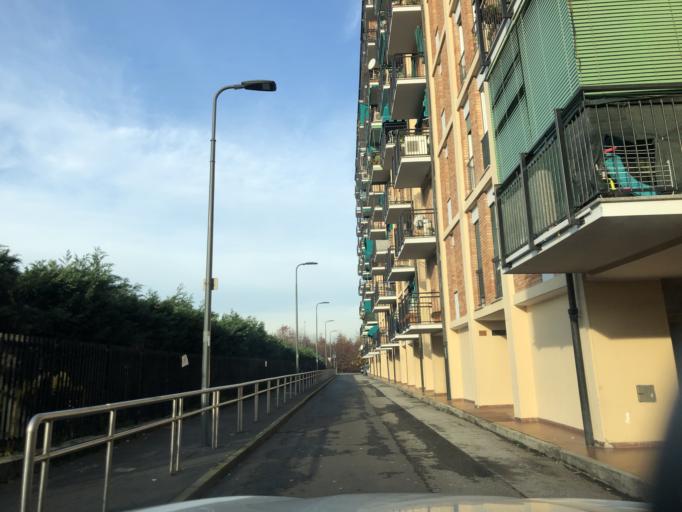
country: IT
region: Lombardy
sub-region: Citta metropolitana di Milano
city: Baranzate
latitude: 45.4928
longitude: 9.1204
